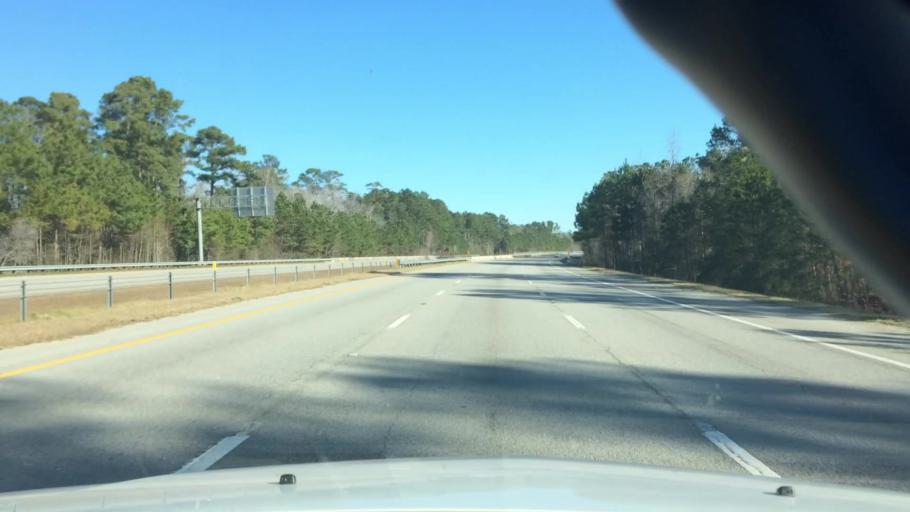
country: US
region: South Carolina
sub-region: Horry County
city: North Myrtle Beach
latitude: 33.8628
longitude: -78.6947
